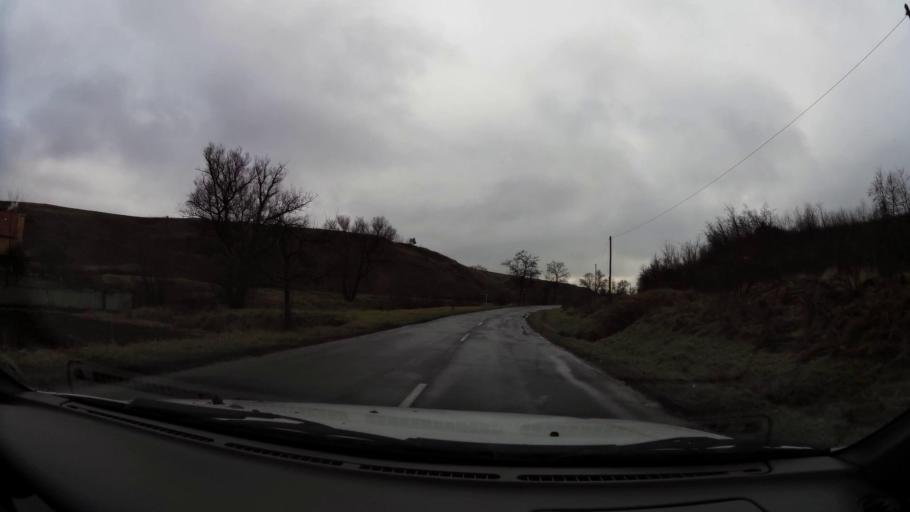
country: HU
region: Borsod-Abauj-Zemplen
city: Izsofalva
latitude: 48.3228
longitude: 20.6510
